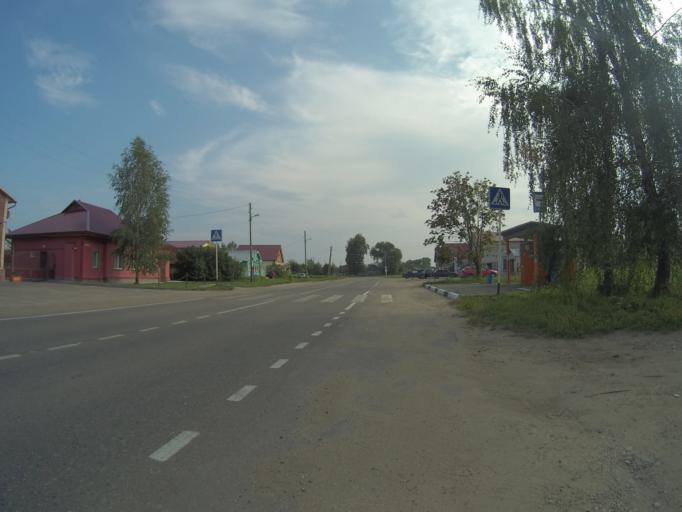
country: RU
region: Vladimir
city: Suzdal'
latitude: 56.4292
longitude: 40.4176
